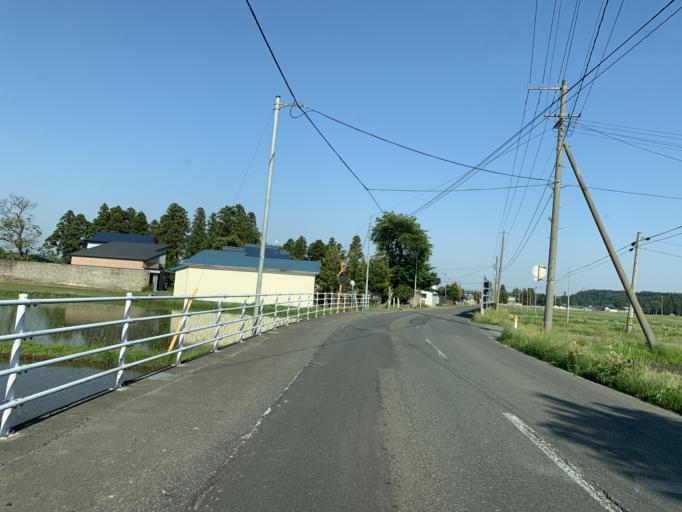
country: JP
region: Iwate
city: Kitakami
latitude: 39.2954
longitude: 140.9858
